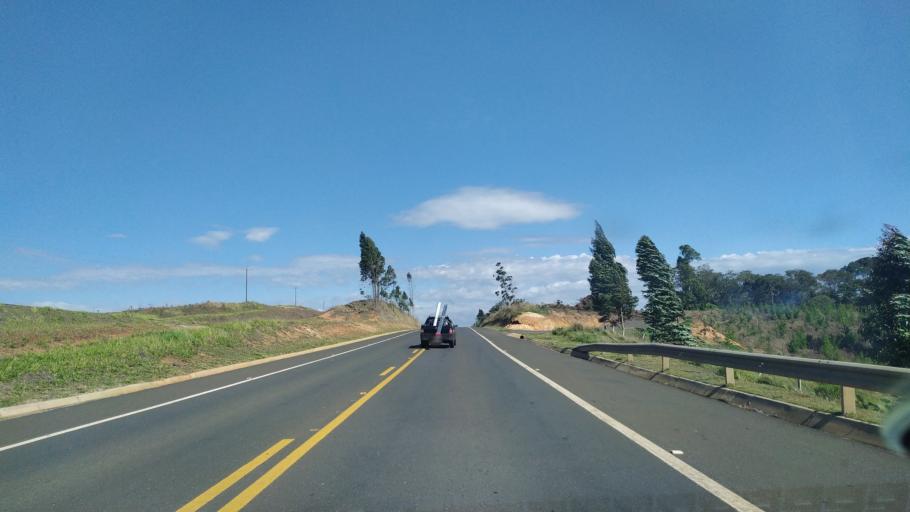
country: BR
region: Parana
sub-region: Ortigueira
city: Ortigueira
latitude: -24.2841
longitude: -50.8110
